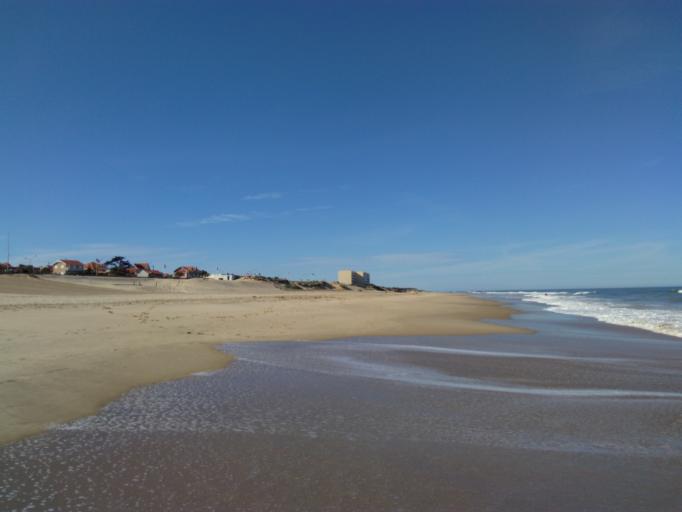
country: FR
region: Aquitaine
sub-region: Departement de la Gironde
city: Soulac-sur-Mer
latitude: 45.5169
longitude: -1.1292
